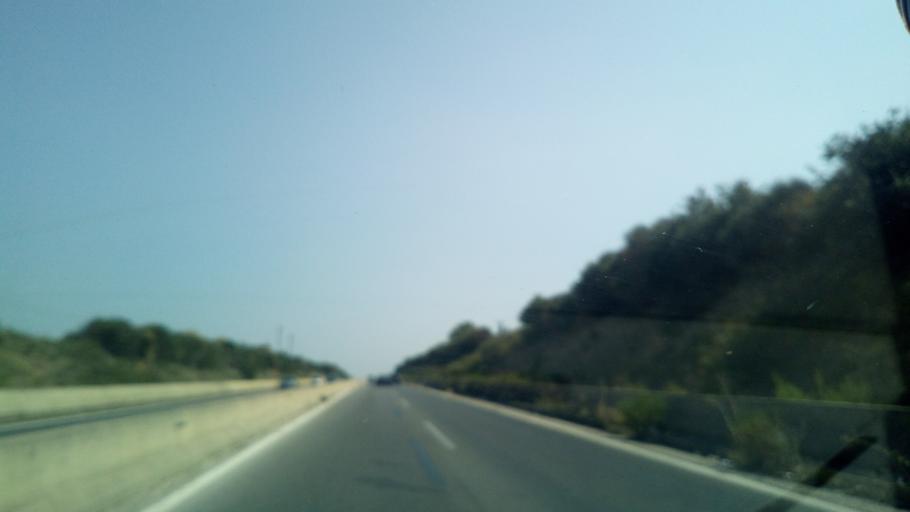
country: GR
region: Central Macedonia
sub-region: Nomos Chalkidikis
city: Nea Kallikrateia
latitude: 40.3019
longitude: 23.1341
